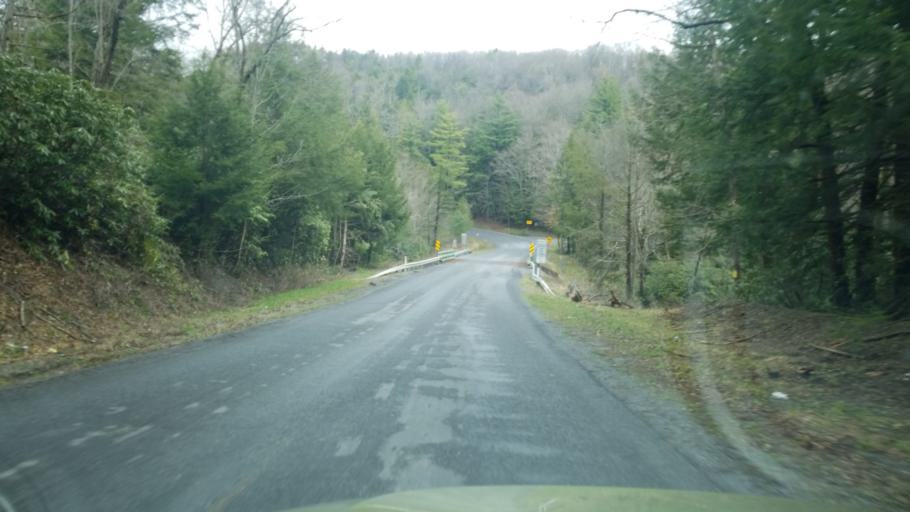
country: US
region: Pennsylvania
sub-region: Clearfield County
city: Clearfield
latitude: 41.0632
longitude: -78.4184
